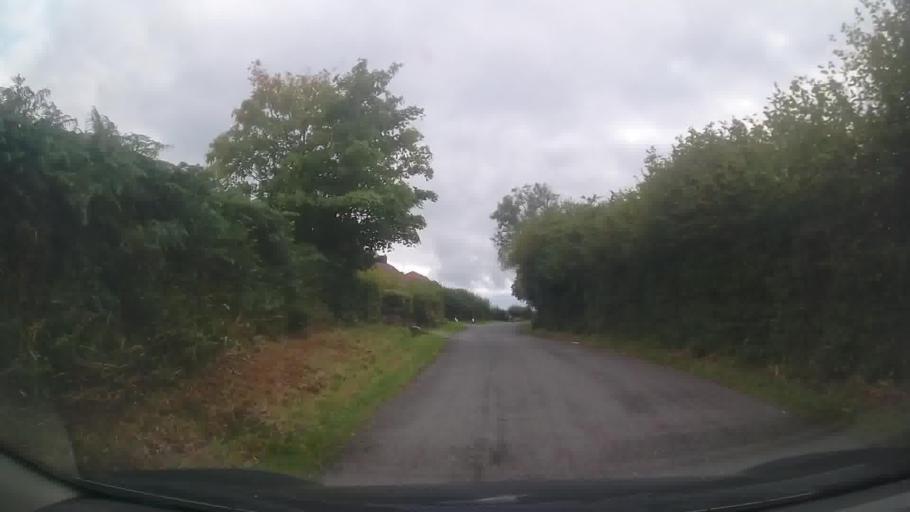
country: GB
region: Wales
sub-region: Carmarthenshire
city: Whitland
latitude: 51.7593
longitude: -4.6367
